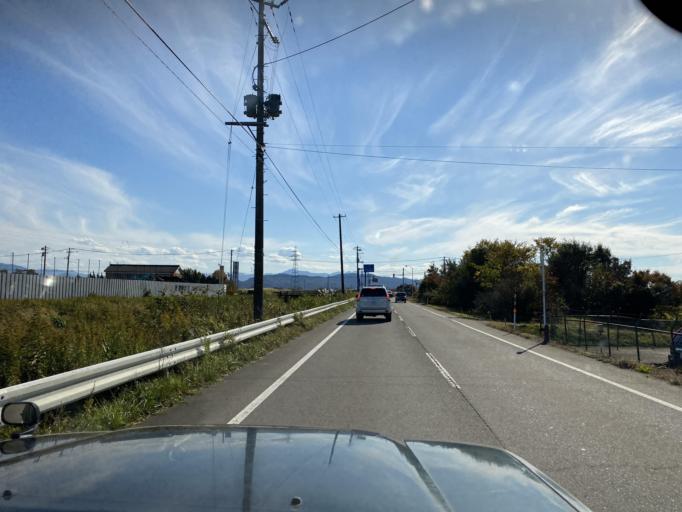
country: JP
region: Niigata
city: Niitsu-honcho
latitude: 37.7922
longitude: 139.0797
